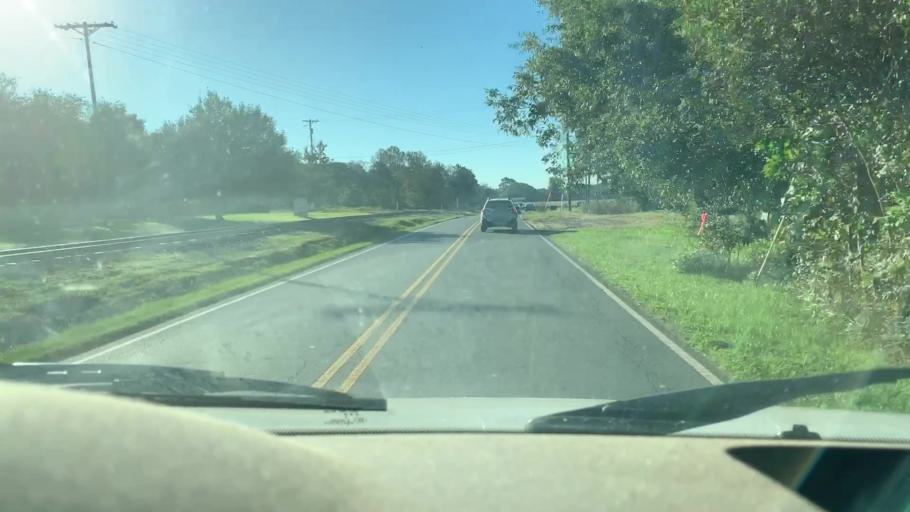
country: US
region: North Carolina
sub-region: Mecklenburg County
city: Cornelius
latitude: 35.4599
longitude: -80.8439
